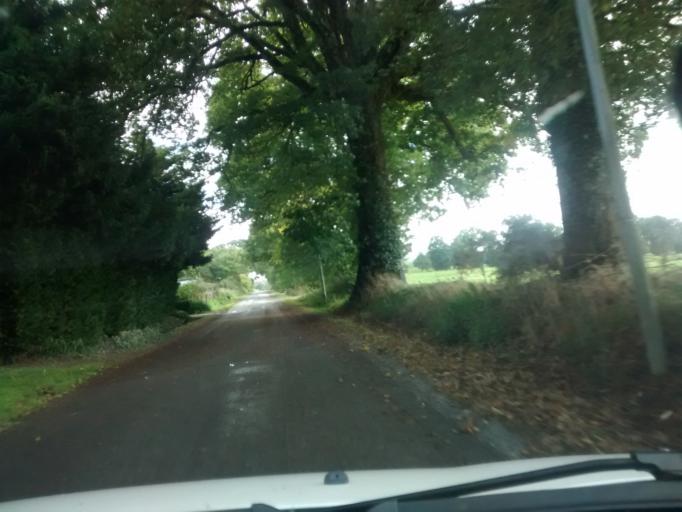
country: FR
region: Brittany
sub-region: Departement d'Ille-et-Vilaine
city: Chateaubourg
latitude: 48.1301
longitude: -1.4064
